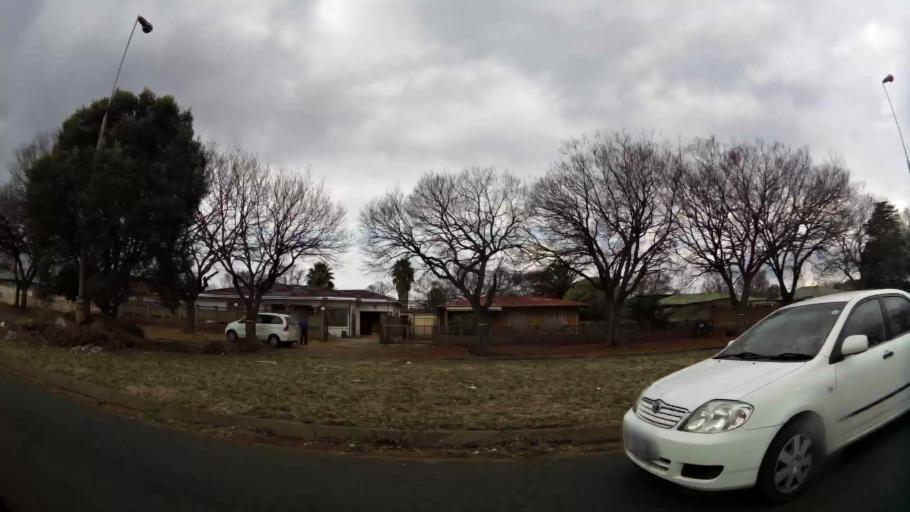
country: ZA
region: Gauteng
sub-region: Sedibeng District Municipality
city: Vanderbijlpark
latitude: -26.6994
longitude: 27.8227
